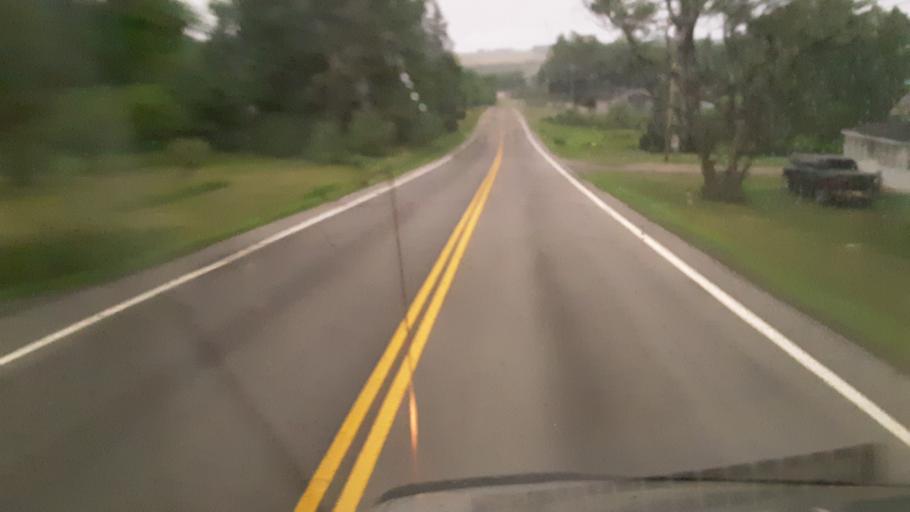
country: US
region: Maine
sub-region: Penobscot County
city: Patten
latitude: 46.0631
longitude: -68.4388
